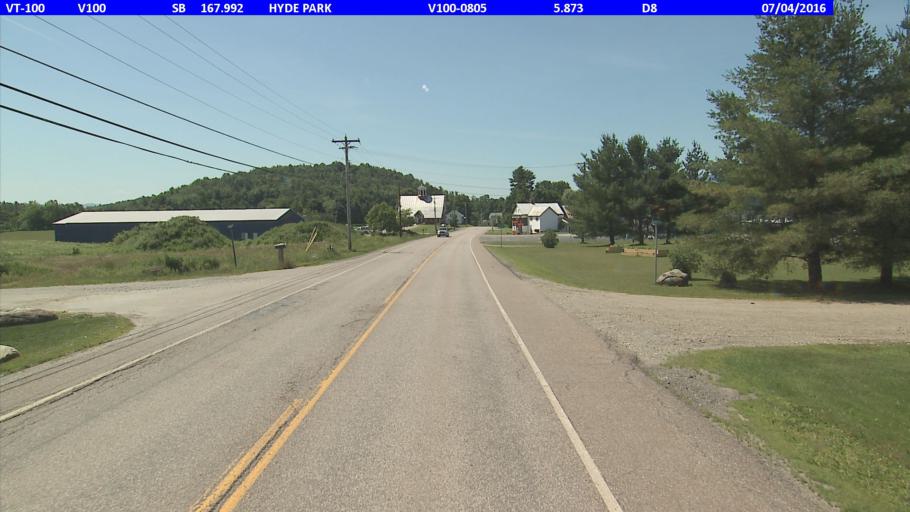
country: US
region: Vermont
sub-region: Lamoille County
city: Hyde Park
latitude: 44.6752
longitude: -72.5954
